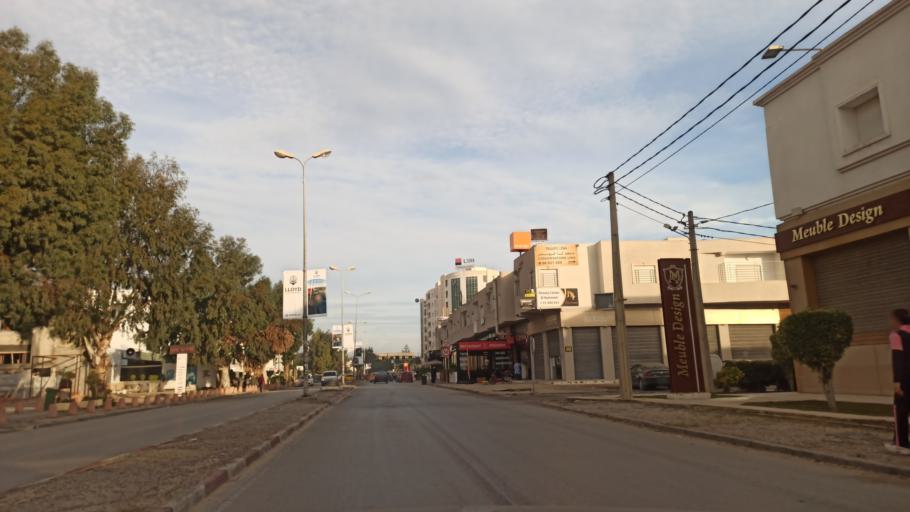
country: TN
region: Tunis
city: La Goulette
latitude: 36.8572
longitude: 10.2566
